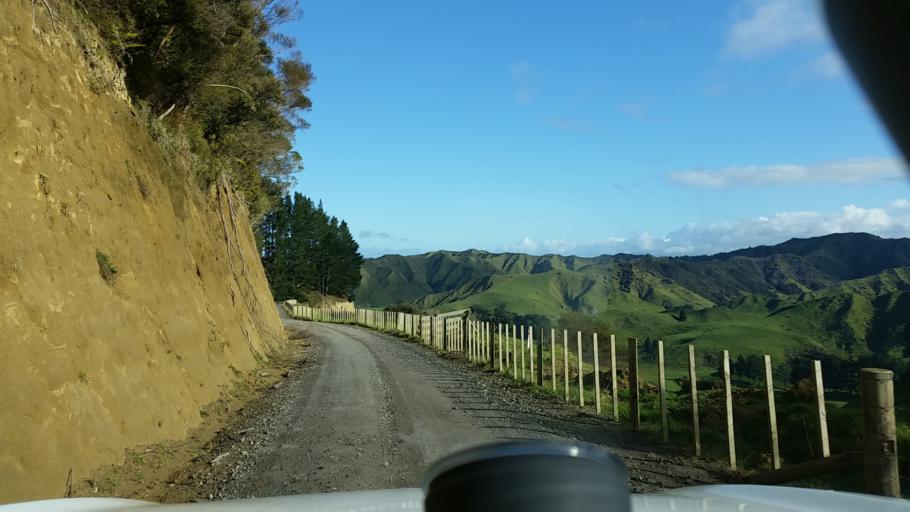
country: NZ
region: Taranaki
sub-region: South Taranaki District
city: Eltham
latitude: -39.4082
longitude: 174.5393
